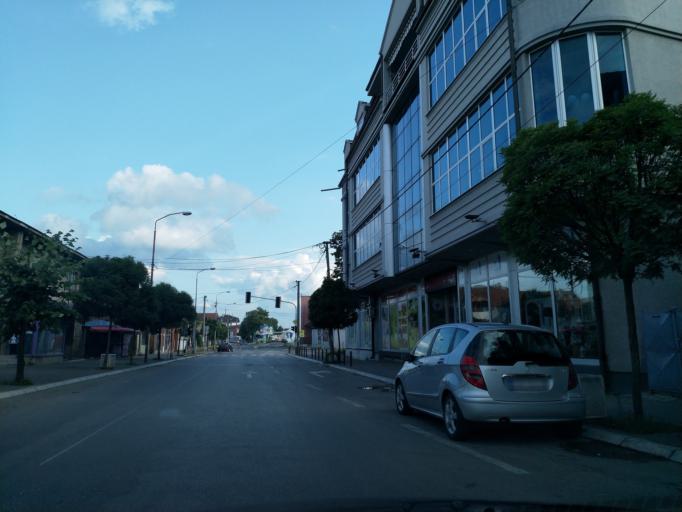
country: RS
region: Central Serbia
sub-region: Pomoravski Okrug
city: Paracin
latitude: 43.8560
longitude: 21.4123
